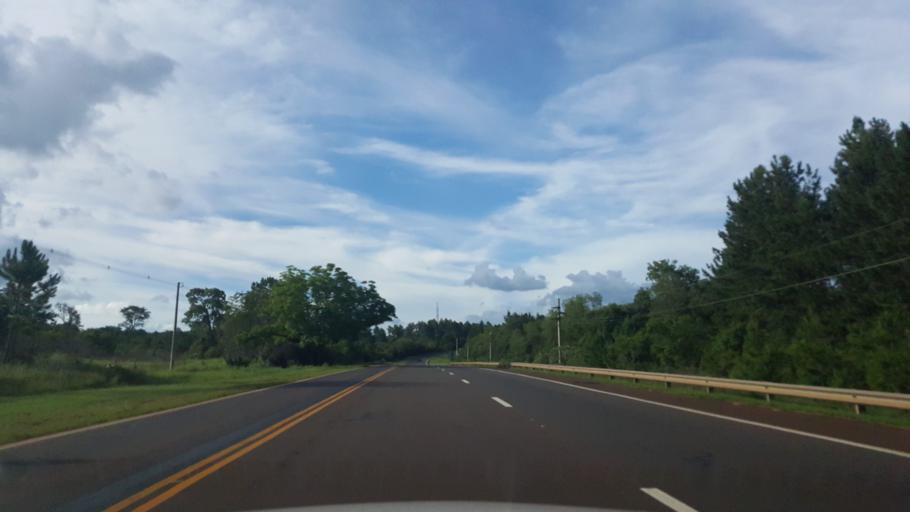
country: AR
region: Misiones
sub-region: Departamento de San Ignacio
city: San Ignacio
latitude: -27.2745
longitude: -55.5387
